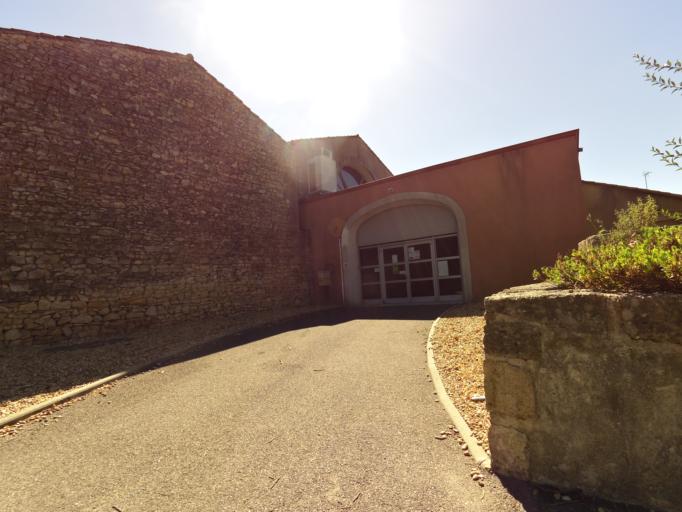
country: FR
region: Languedoc-Roussillon
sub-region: Departement du Gard
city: Codognan
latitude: 43.7349
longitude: 4.2194
